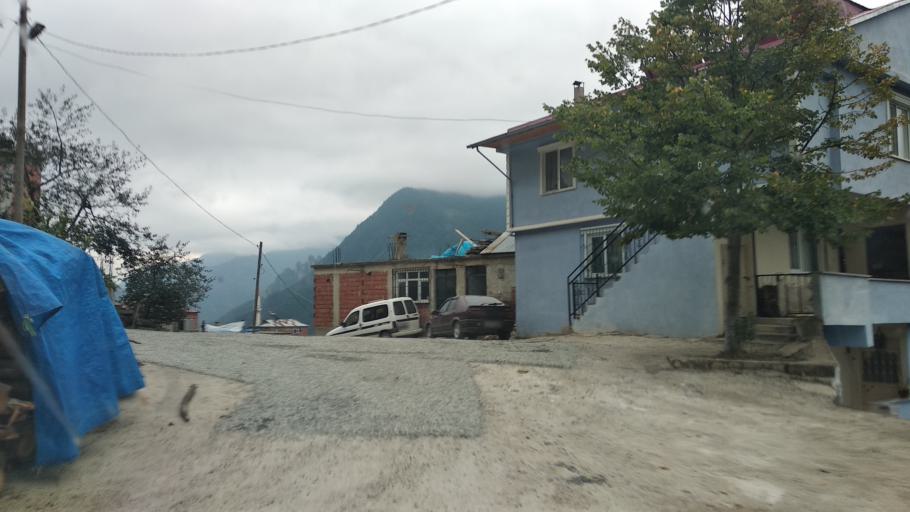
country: TR
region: Giresun
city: Dogankent
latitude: 40.7480
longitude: 38.9852
